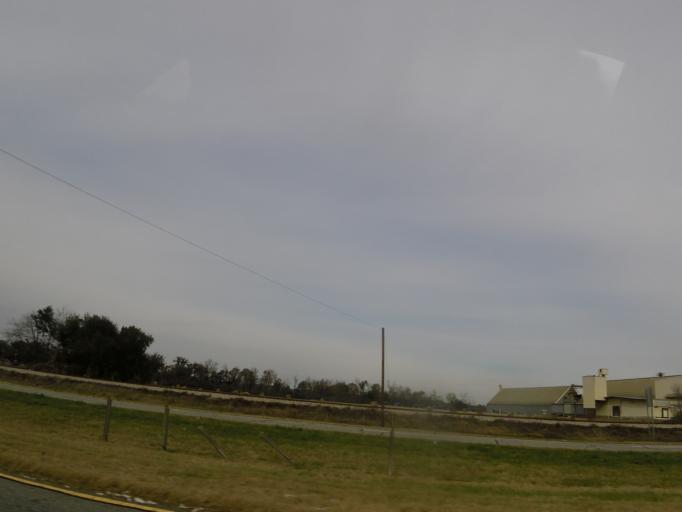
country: US
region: Georgia
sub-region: Seminole County
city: Donalsonville
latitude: 31.0310
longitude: -84.8546
